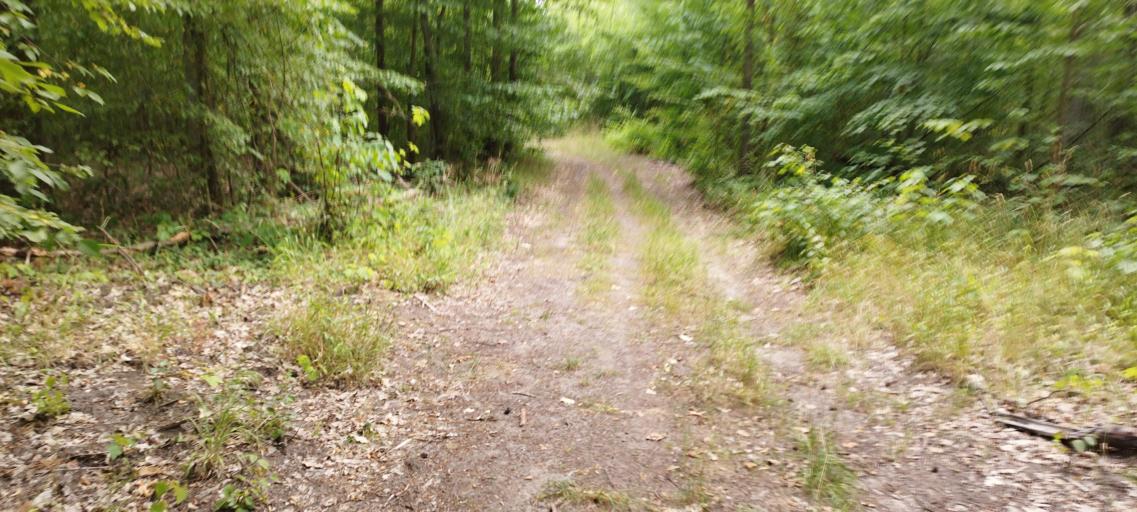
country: DE
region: Brandenburg
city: Woltersdorf
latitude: 52.4531
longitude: 13.7909
